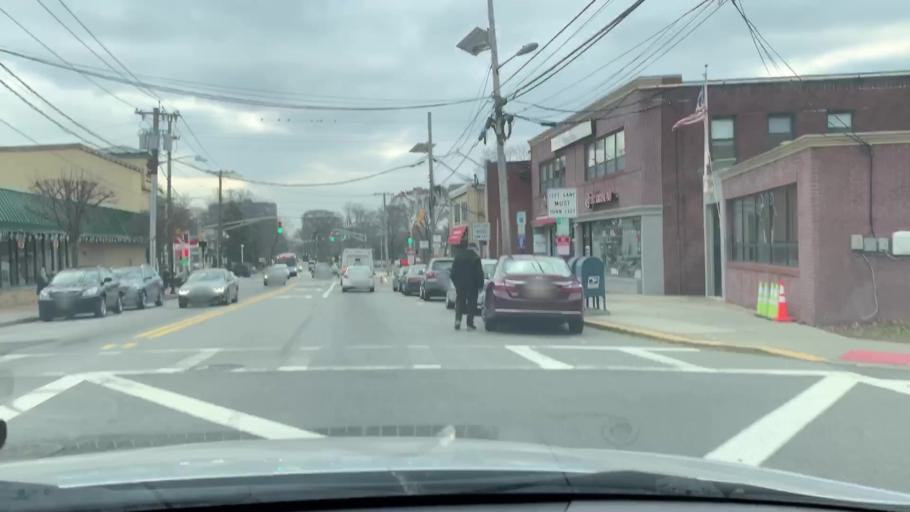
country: US
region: New Jersey
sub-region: Bergen County
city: Edgewater
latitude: 40.8398
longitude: -73.9814
